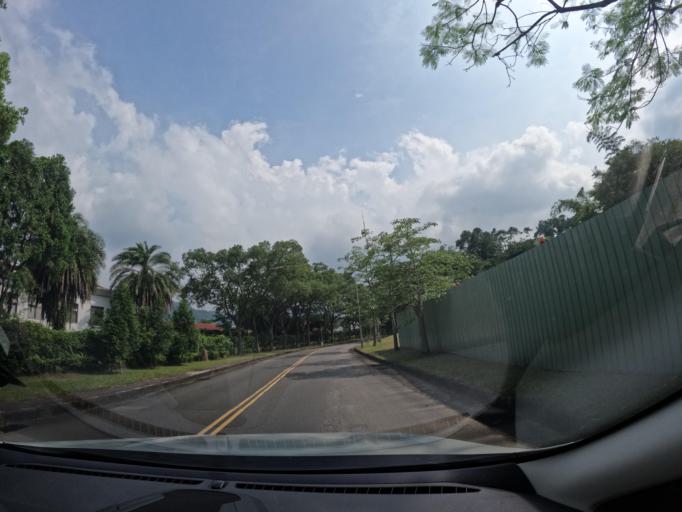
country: TW
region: Taiwan
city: Daxi
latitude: 24.8900
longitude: 121.3227
